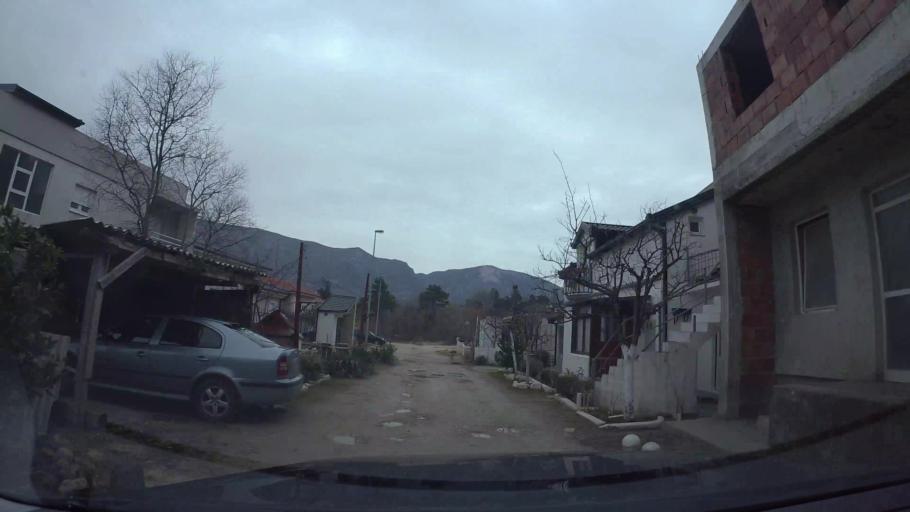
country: BA
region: Federation of Bosnia and Herzegovina
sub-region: Hercegovacko-Bosanski Kanton
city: Mostar
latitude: 43.3499
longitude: 17.8119
